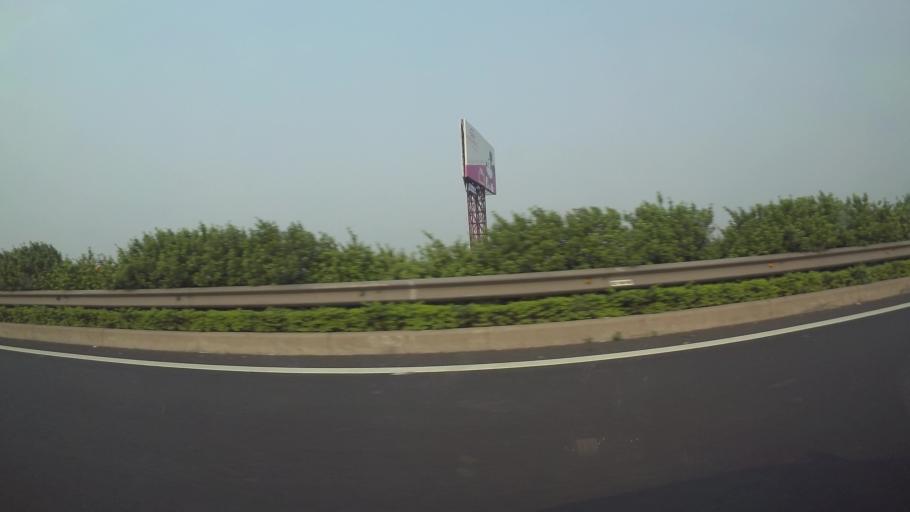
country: VN
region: Ha Noi
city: Thuong Tin
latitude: 20.8914
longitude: 105.8682
